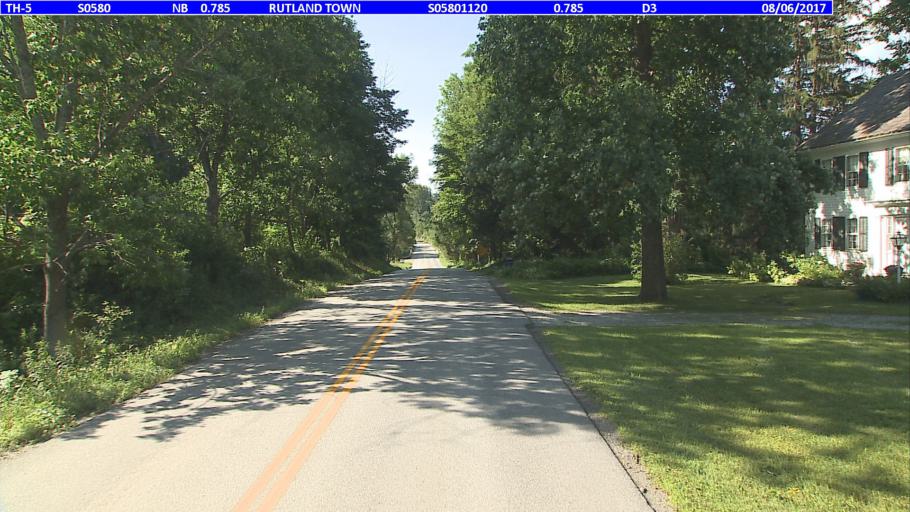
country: US
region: Vermont
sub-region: Rutland County
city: Rutland
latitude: 43.5748
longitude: -72.9515
